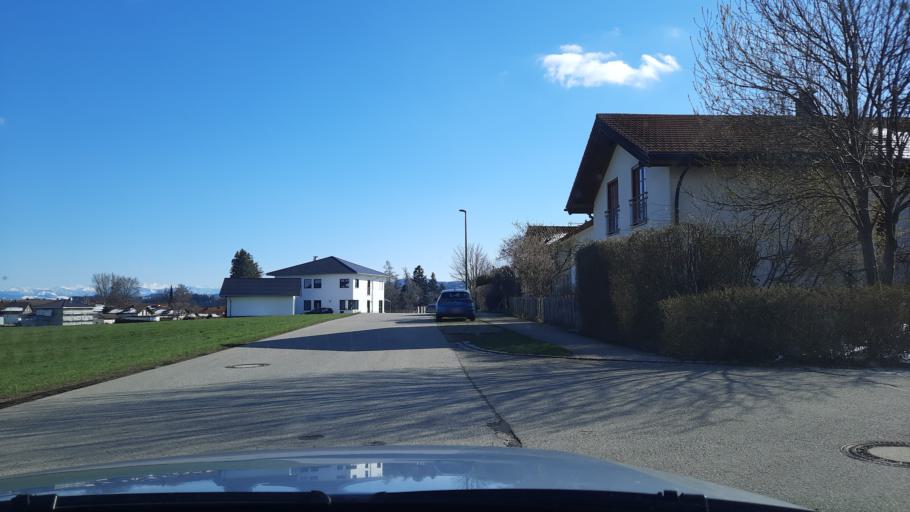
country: DE
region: Bavaria
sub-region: Swabia
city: Altusried
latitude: 47.8094
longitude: 10.2141
